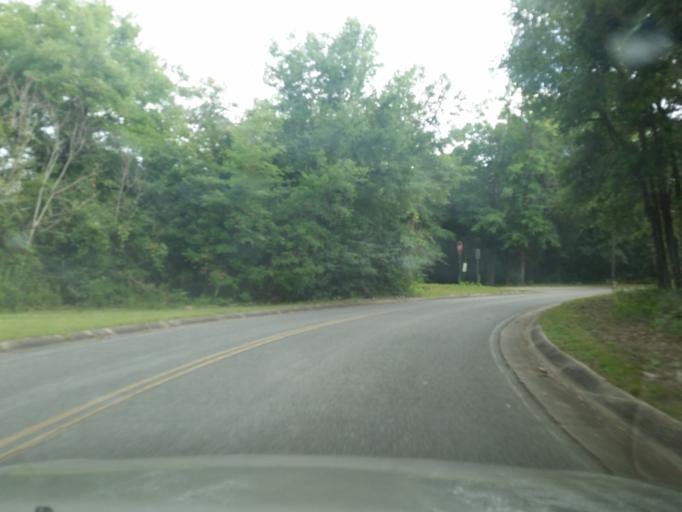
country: US
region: Florida
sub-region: Escambia County
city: Ferry Pass
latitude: 30.5430
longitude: -87.1995
